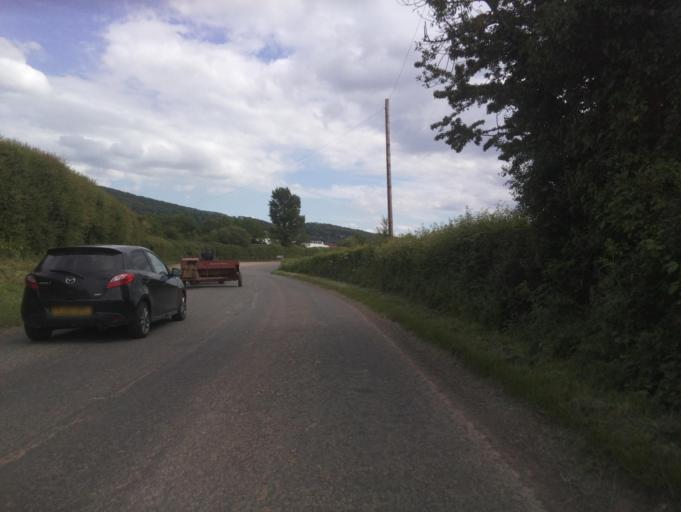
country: GB
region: England
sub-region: Herefordshire
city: Ledbury
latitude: 52.0562
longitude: -2.4411
